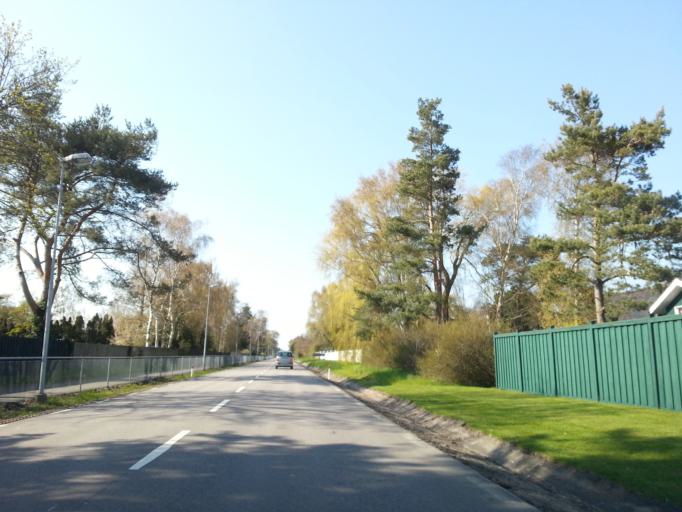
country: SE
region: Skane
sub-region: Vellinge Kommun
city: Hollviken
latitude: 55.4062
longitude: 12.9831
